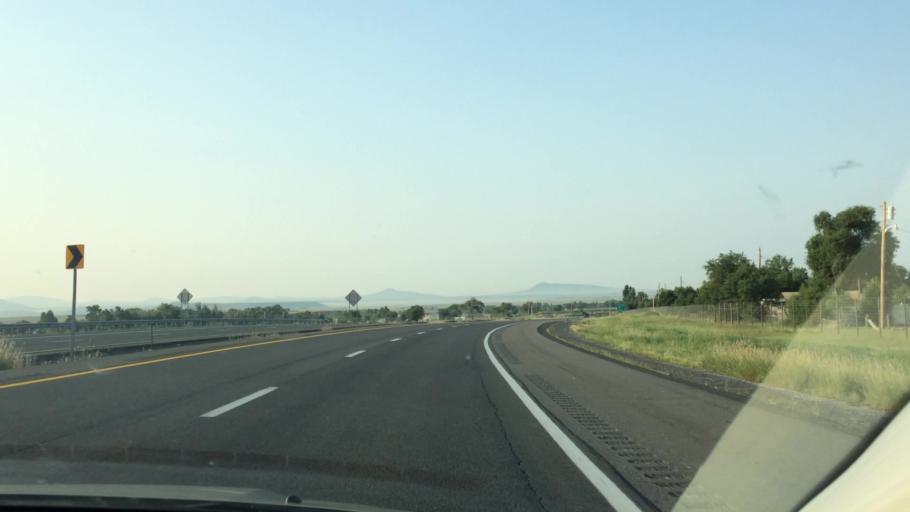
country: US
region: New Mexico
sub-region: Colfax County
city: Raton
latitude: 36.9079
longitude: -104.4245
